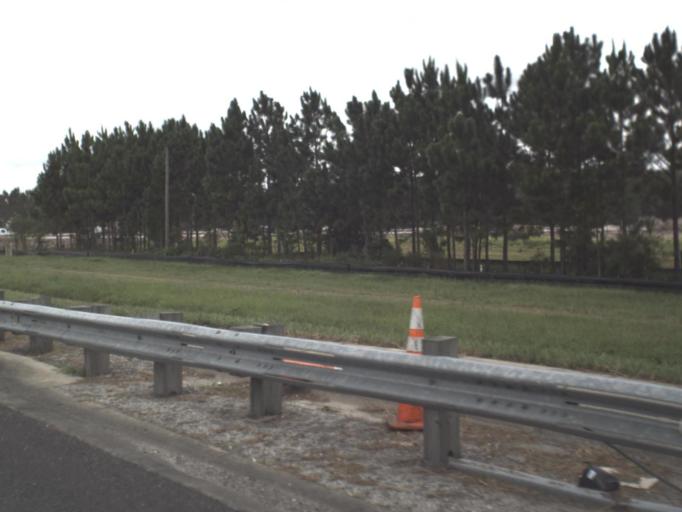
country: US
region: Florida
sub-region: Pasco County
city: Odessa
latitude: 28.1909
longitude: -82.6128
